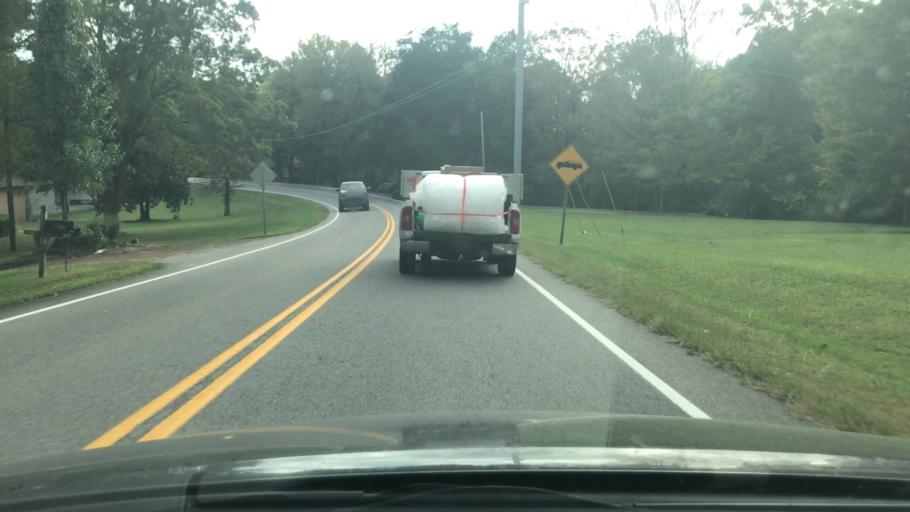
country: US
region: Tennessee
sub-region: Cheatham County
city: Ashland City
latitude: 36.2844
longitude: -87.1812
